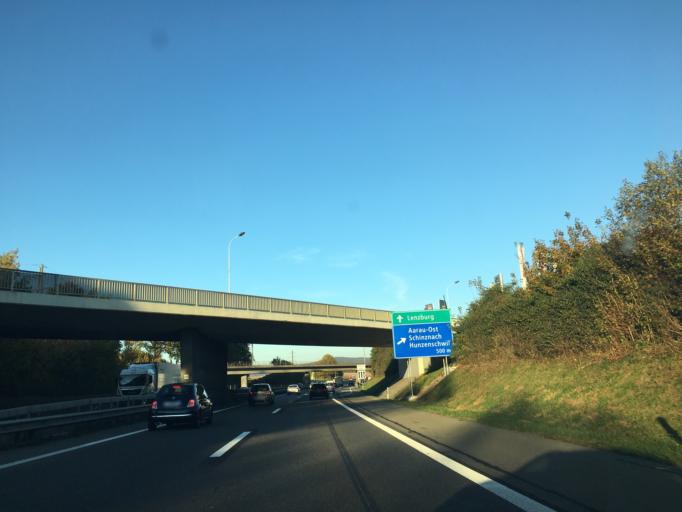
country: CH
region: Aargau
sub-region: Bezirk Brugg
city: Rupperswil
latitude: 47.3869
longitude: 8.1163
